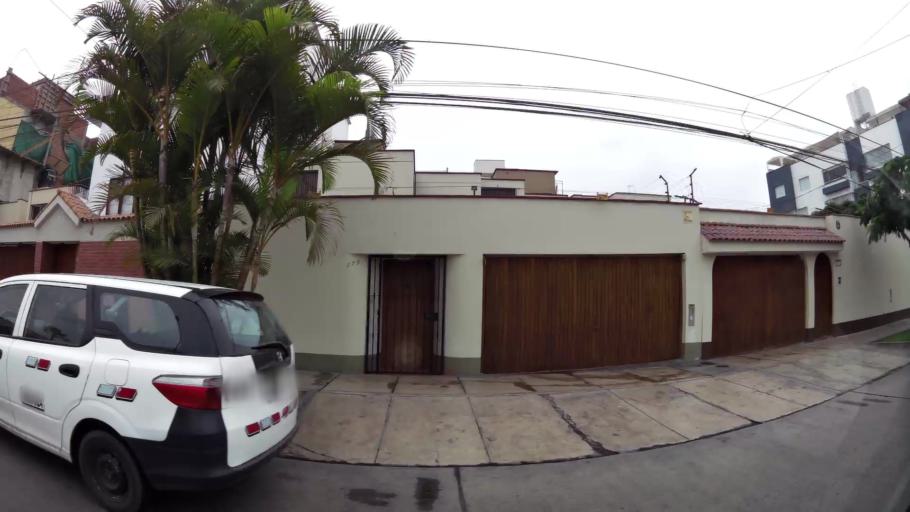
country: PE
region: Lima
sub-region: Lima
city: Surco
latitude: -12.1312
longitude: -77.0071
